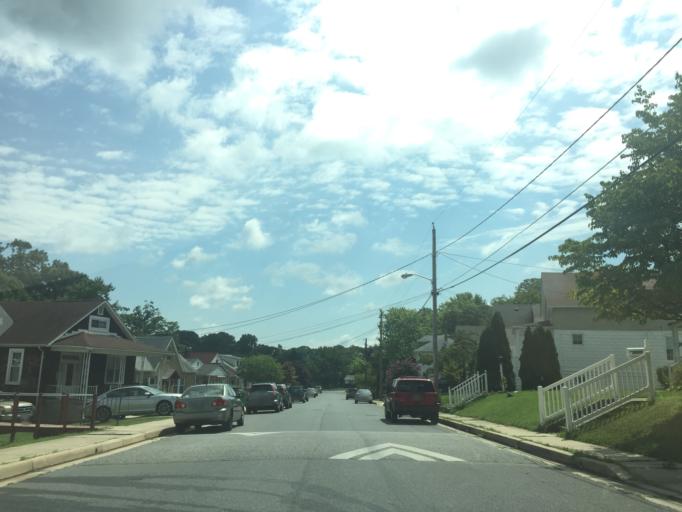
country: US
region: Maryland
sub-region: Baltimore County
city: Carney
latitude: 39.3844
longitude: -76.5266
